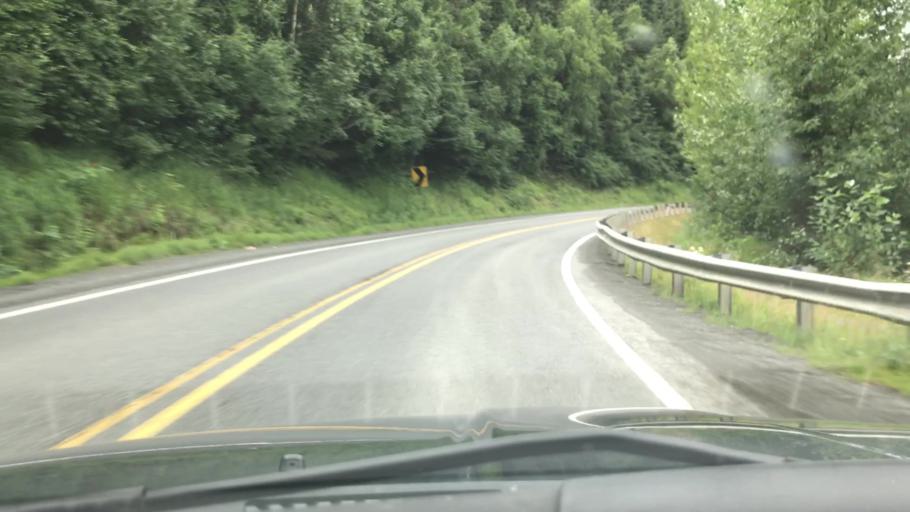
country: US
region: Alaska
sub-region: Kenai Peninsula Borough
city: Seward
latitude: 60.4853
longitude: -149.8543
